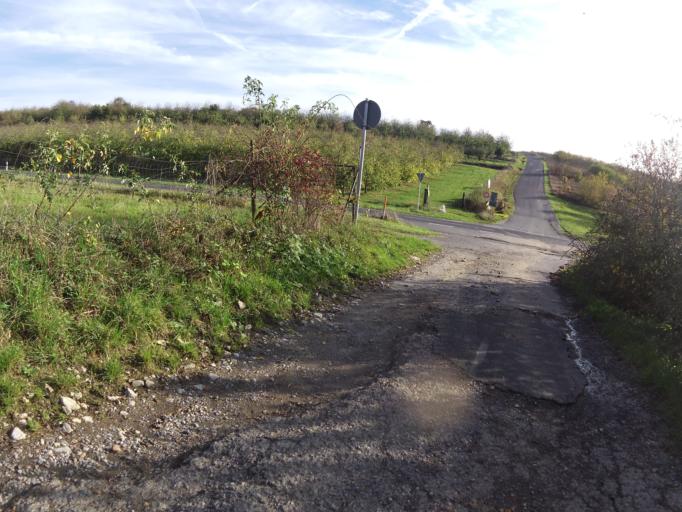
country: DE
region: Bavaria
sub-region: Regierungsbezirk Unterfranken
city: Sommerhausen
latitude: 49.7108
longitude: 10.0393
